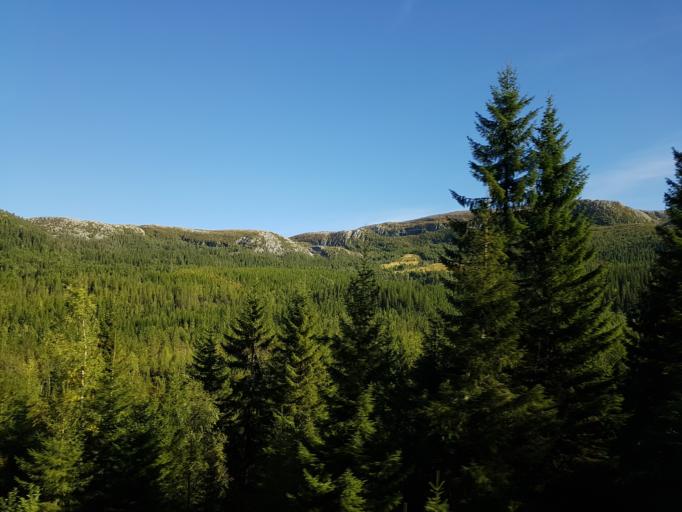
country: NO
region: Sor-Trondelag
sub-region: Afjord
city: A i Afjord
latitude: 63.7274
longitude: 10.2353
